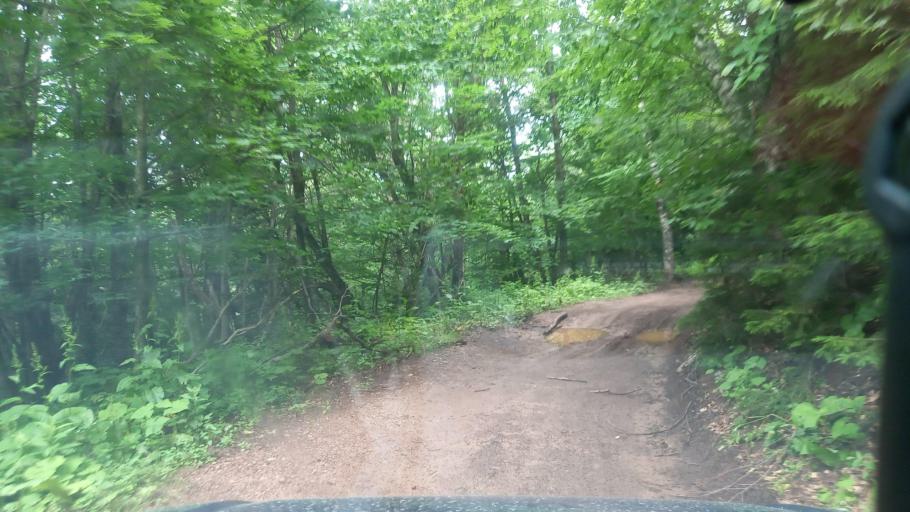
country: RU
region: Karachayevo-Cherkesiya
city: Kurdzhinovo
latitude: 43.8086
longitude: 40.8549
